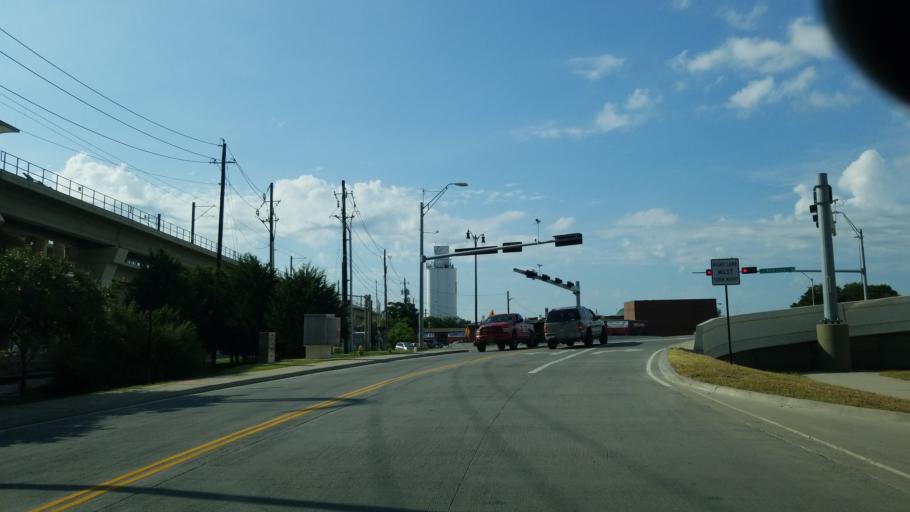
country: US
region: Texas
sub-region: Dallas County
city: Carrollton
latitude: 32.9543
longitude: -96.9085
